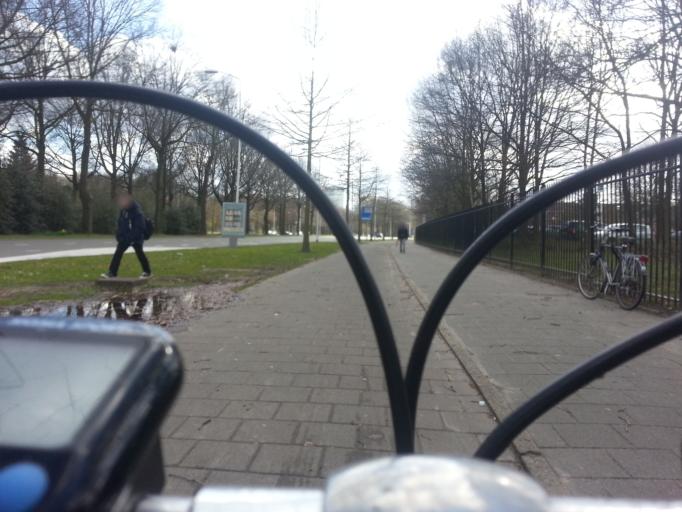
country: NL
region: North Brabant
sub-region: Gemeente Eindhoven
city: Eindhoven
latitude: 51.4521
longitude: 5.4838
